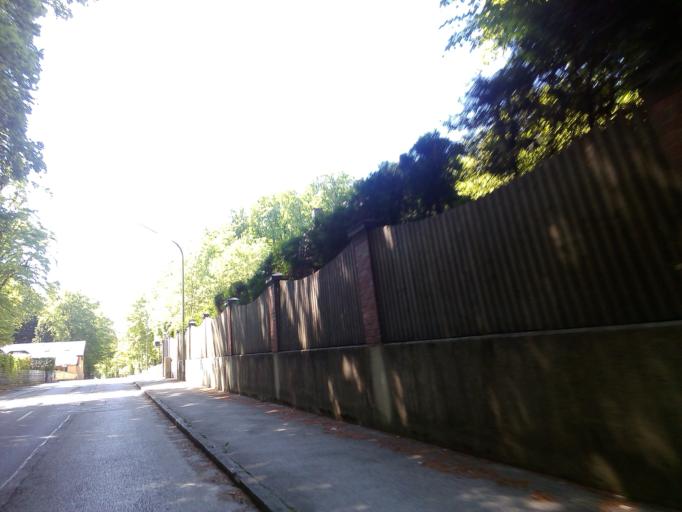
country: DE
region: Bavaria
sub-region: Upper Bavaria
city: Starnberg
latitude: 47.9798
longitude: 11.3305
